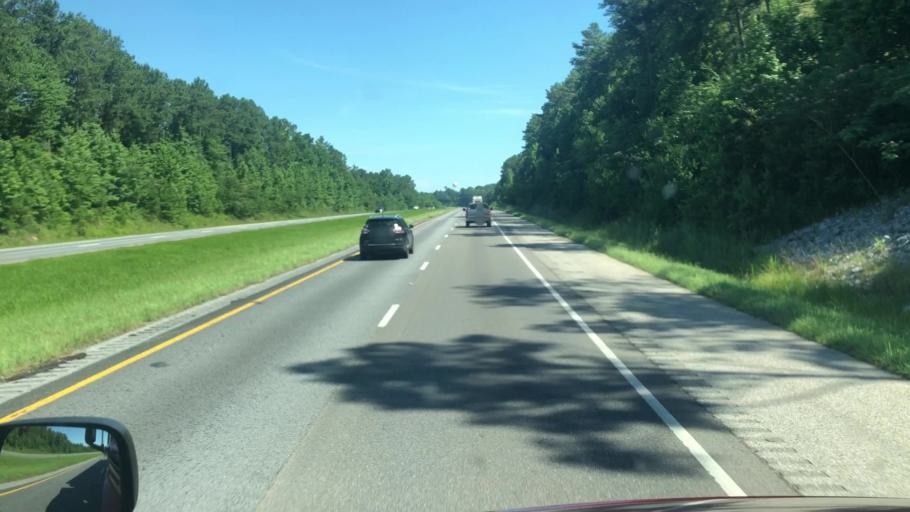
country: US
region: Alabama
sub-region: Autauga County
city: Pine Level
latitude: 32.5990
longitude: -86.4779
